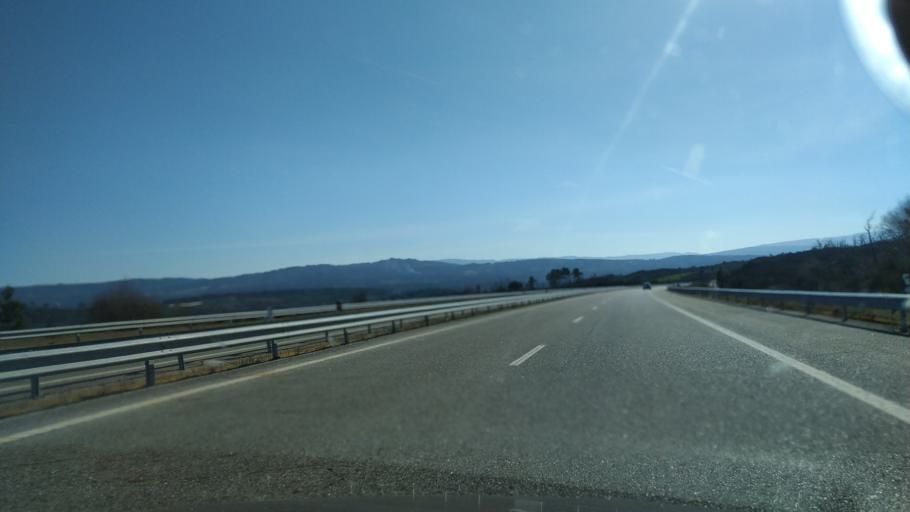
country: PT
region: Vila Real
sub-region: Chaves
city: Chaves
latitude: 41.7410
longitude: -7.5249
